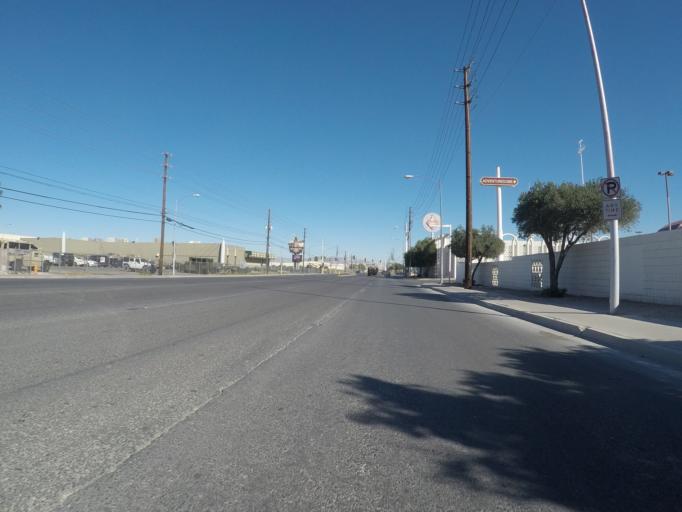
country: US
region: Nevada
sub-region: Clark County
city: Paradise
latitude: 36.1380
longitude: -115.1686
